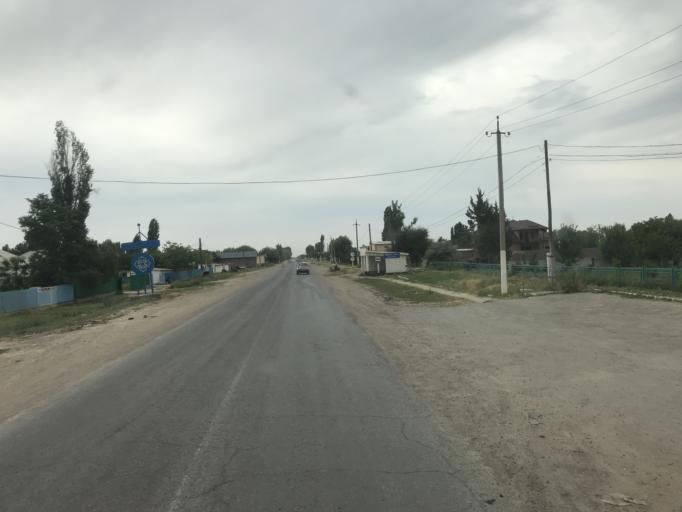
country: KZ
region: Ongtustik Qazaqstan
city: Asykata
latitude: 40.9021
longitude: 68.3578
